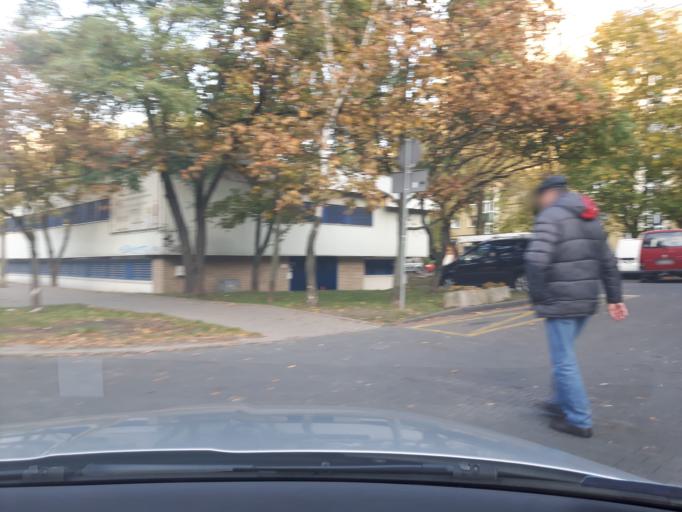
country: PL
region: Masovian Voivodeship
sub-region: Warszawa
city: Ursynow
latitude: 52.1541
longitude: 21.0315
